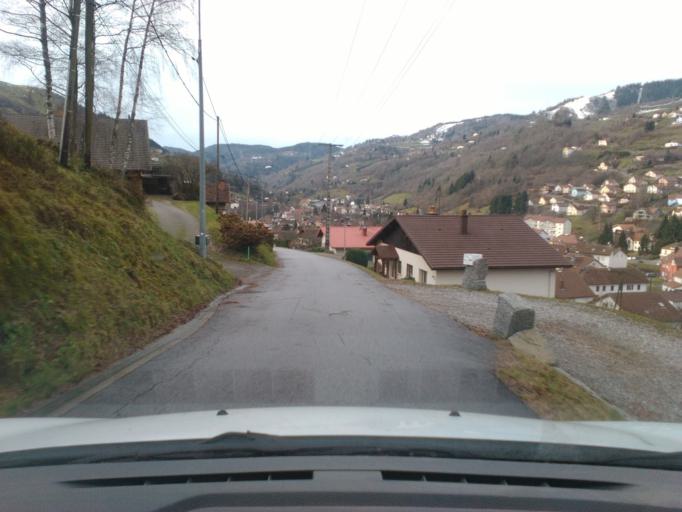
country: FR
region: Lorraine
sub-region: Departement des Vosges
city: La Bresse
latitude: 48.0025
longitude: 6.8781
